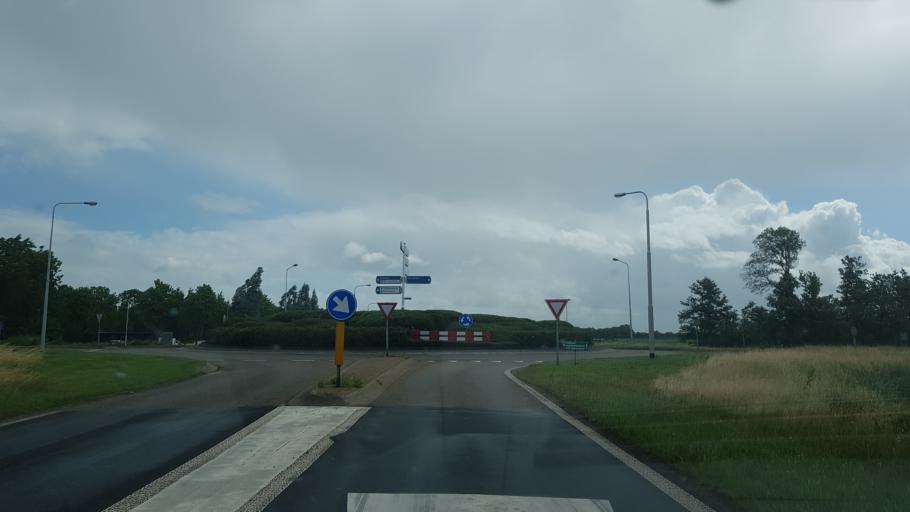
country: NL
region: Friesland
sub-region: Gemeente Dongeradeel
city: Dokkum
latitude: 53.3107
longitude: 5.9928
